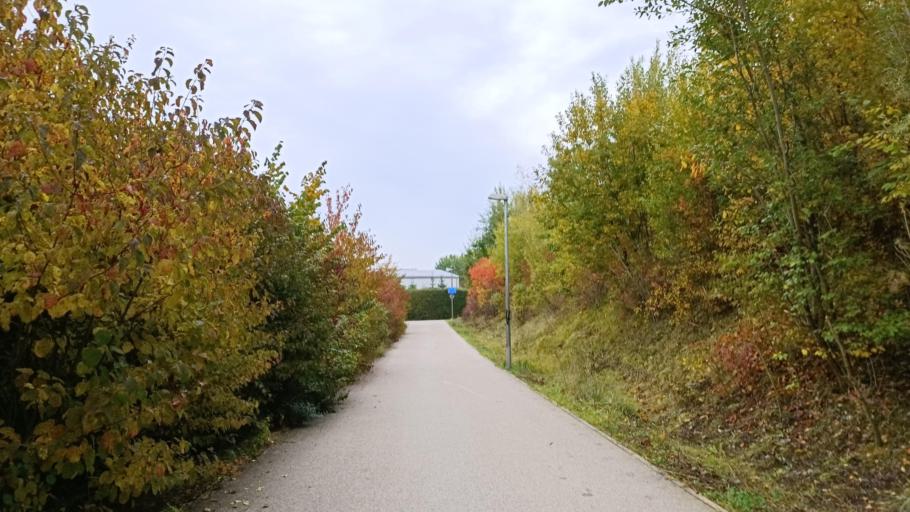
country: DE
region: Bavaria
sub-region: Swabia
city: Augsburg
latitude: 48.3363
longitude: 10.8840
